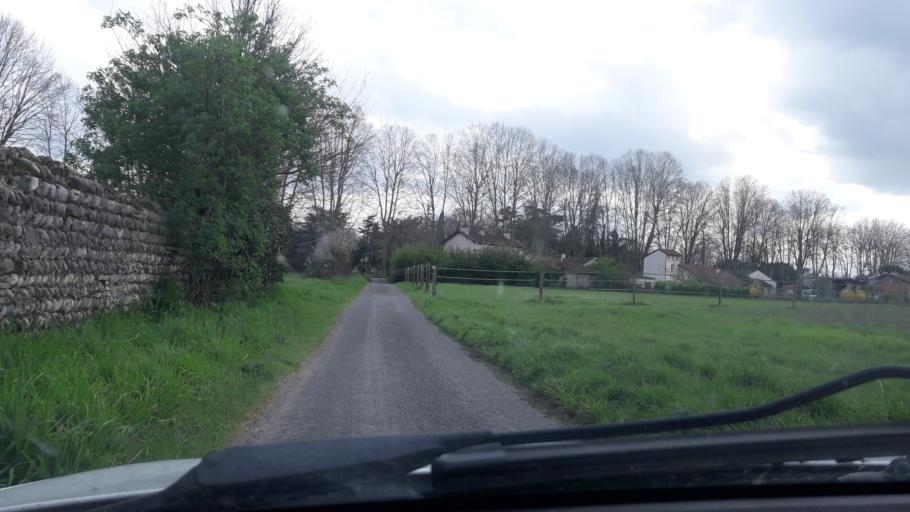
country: FR
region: Midi-Pyrenees
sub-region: Departement de la Haute-Garonne
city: Carbonne
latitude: 43.2932
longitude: 1.2198
